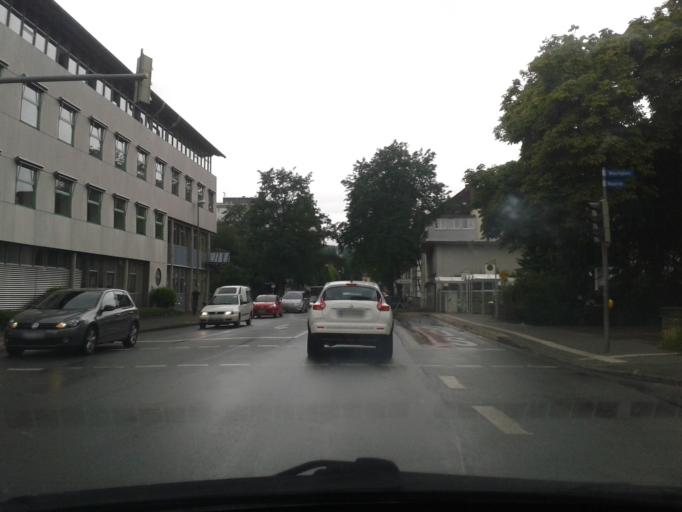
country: DE
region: North Rhine-Westphalia
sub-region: Regierungsbezirk Detmold
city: Detmold
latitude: 51.9347
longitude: 8.8828
